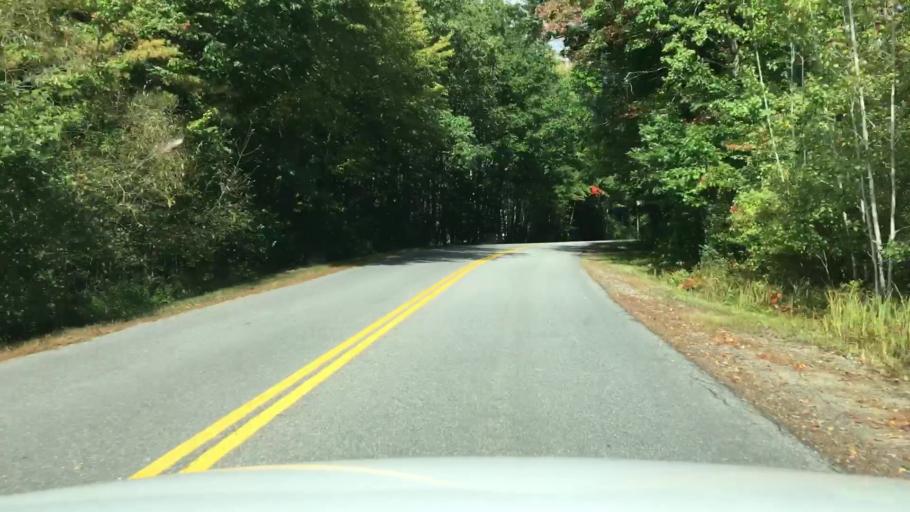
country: US
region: Maine
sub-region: Cumberland County
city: Brunswick
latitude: 43.9565
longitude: -69.8955
